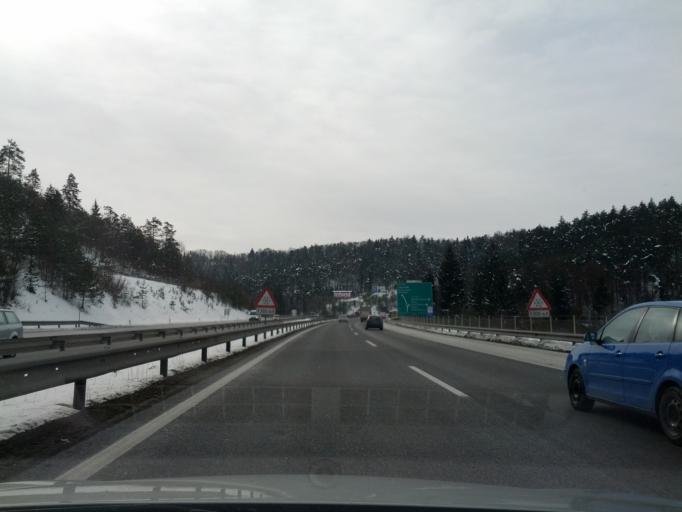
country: SI
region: Skofljica
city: Lavrica
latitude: 46.0263
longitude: 14.5670
